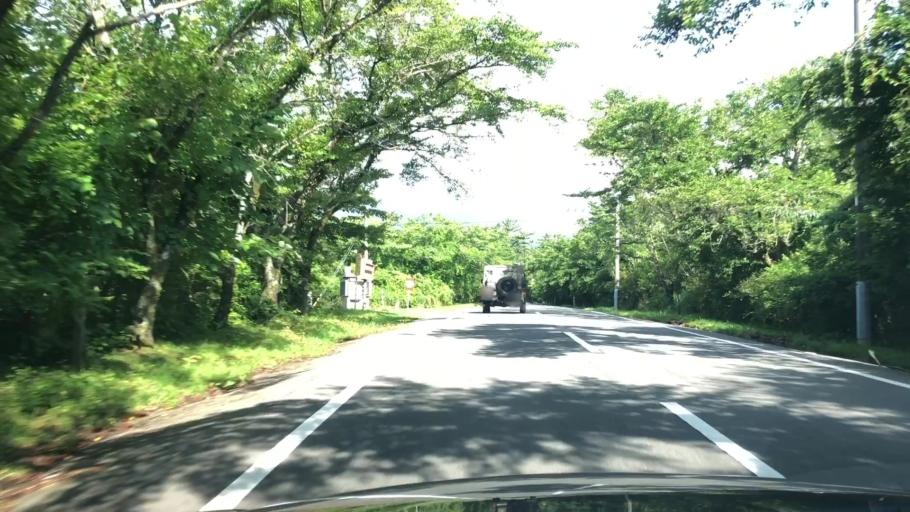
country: JP
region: Shizuoka
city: Gotemba
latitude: 35.3286
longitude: 138.8460
